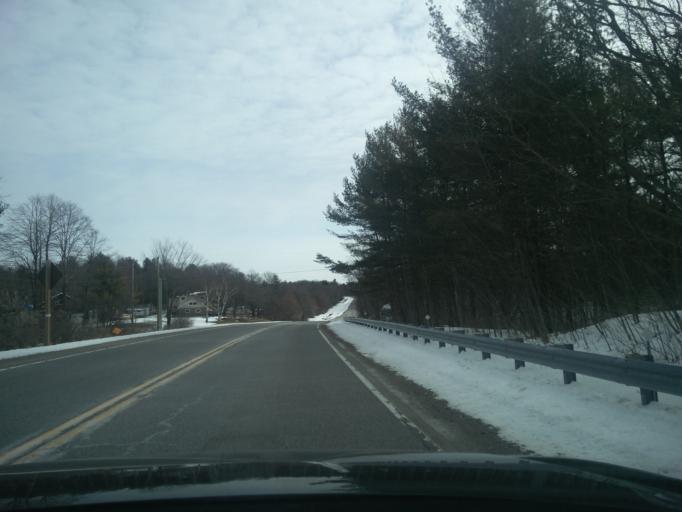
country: US
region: New York
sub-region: Jefferson County
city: Alexandria Bay
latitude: 44.3747
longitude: -75.9511
